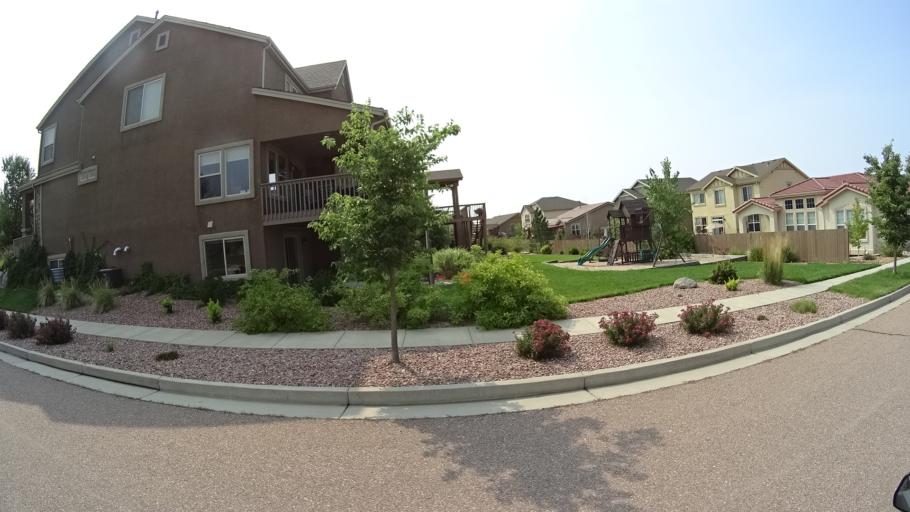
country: US
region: Colorado
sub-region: El Paso County
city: Black Forest
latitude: 38.9660
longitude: -104.7301
